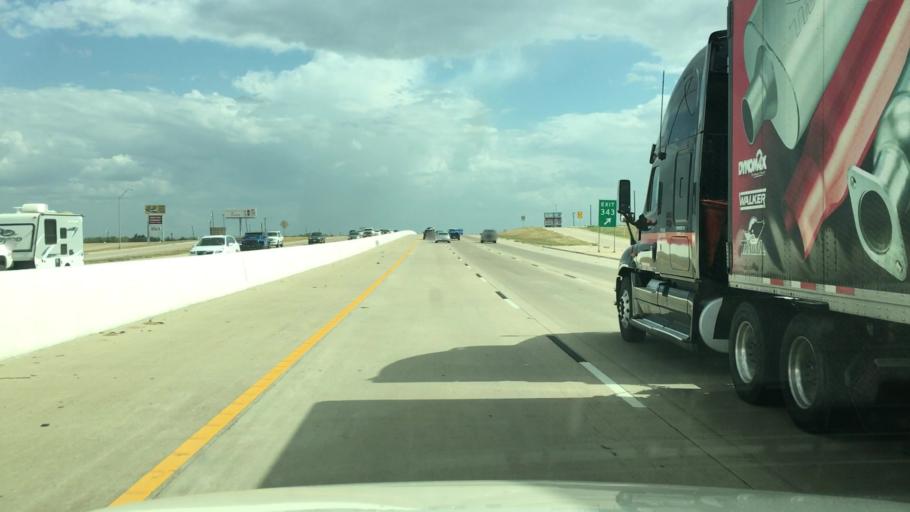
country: US
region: Texas
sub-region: McLennan County
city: Northcrest
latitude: 31.6836
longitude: -97.0999
